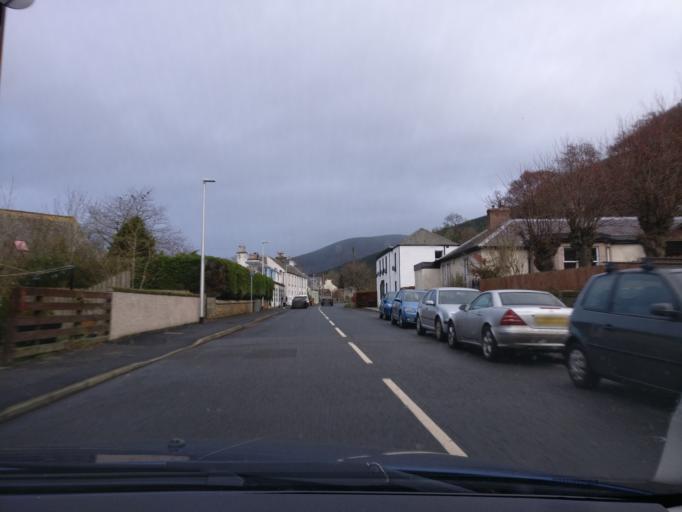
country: GB
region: Scotland
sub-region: The Scottish Borders
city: Innerleithen
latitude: 55.6231
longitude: -3.0611
